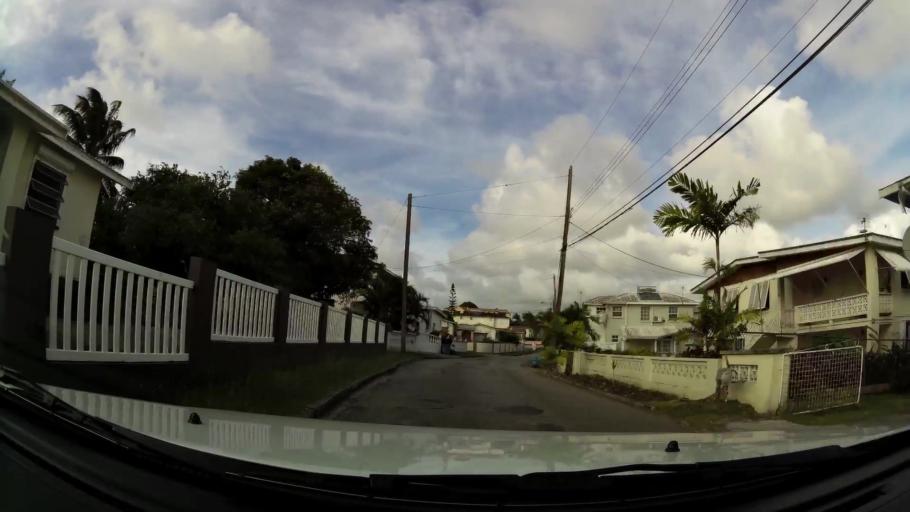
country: BB
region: Christ Church
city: Oistins
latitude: 13.0897
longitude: -59.5704
